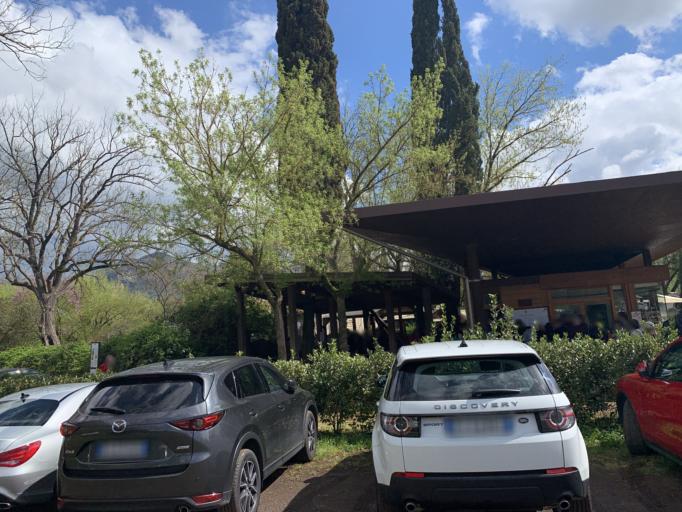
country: IT
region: Latium
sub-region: Provincia di Latina
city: Norma
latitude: 41.5833
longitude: 12.9524
